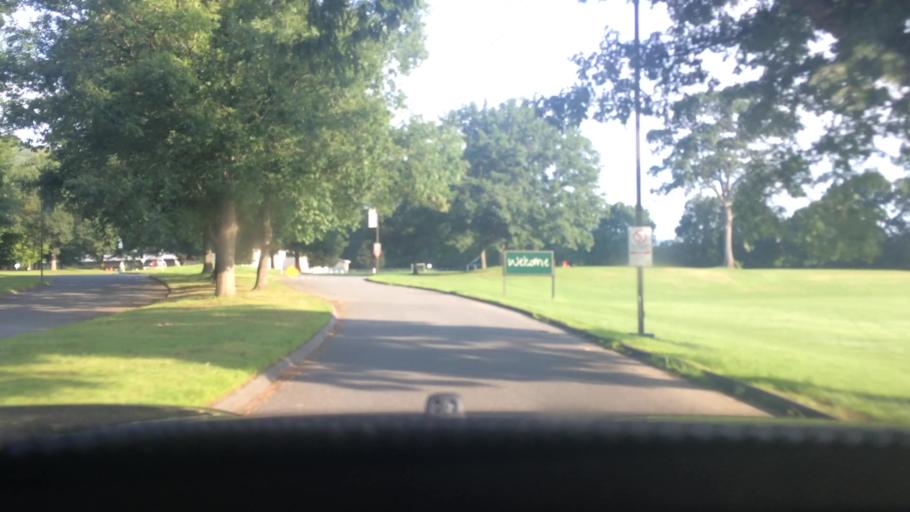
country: US
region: Massachusetts
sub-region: Franklin County
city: Greenfield
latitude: 42.5984
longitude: -72.6255
